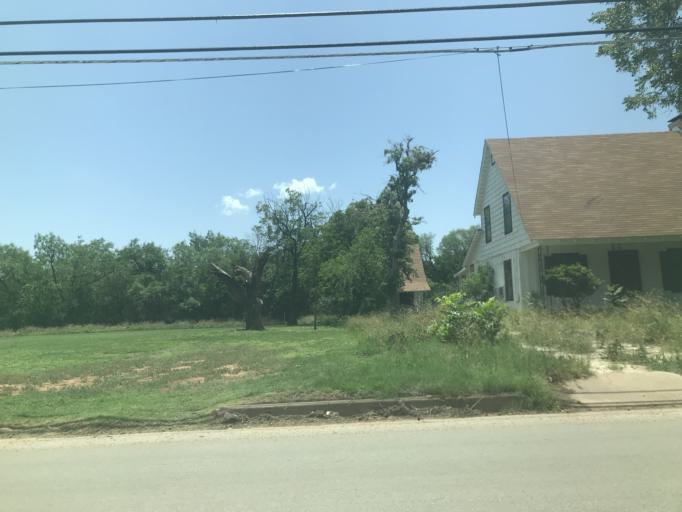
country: US
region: Texas
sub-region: Taylor County
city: Abilene
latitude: 32.4643
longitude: -99.7190
